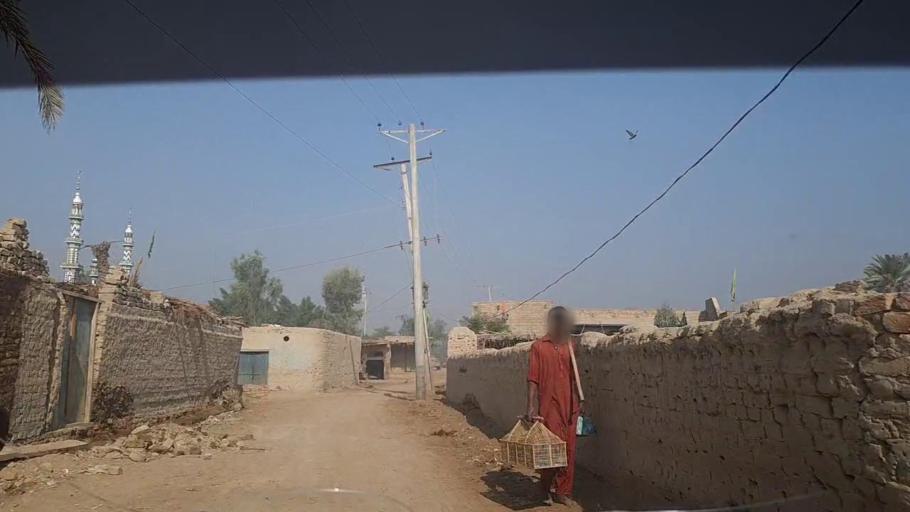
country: PK
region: Sindh
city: Khairpur
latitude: 27.4696
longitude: 68.7132
